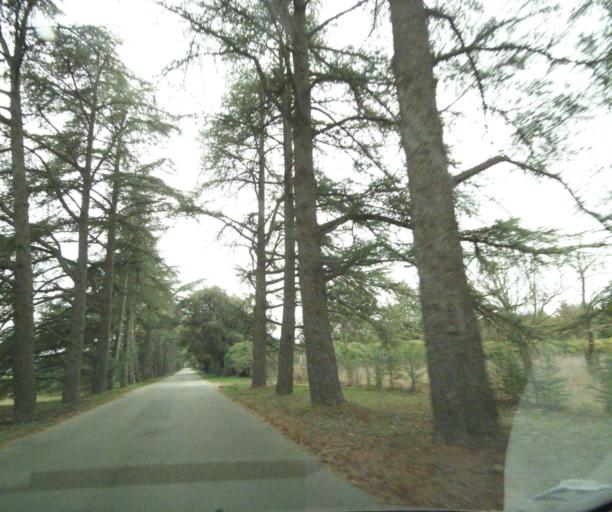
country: FR
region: Provence-Alpes-Cote d'Azur
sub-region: Departement du Var
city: Vinon-sur-Verdon
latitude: 43.7123
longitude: 5.7577
